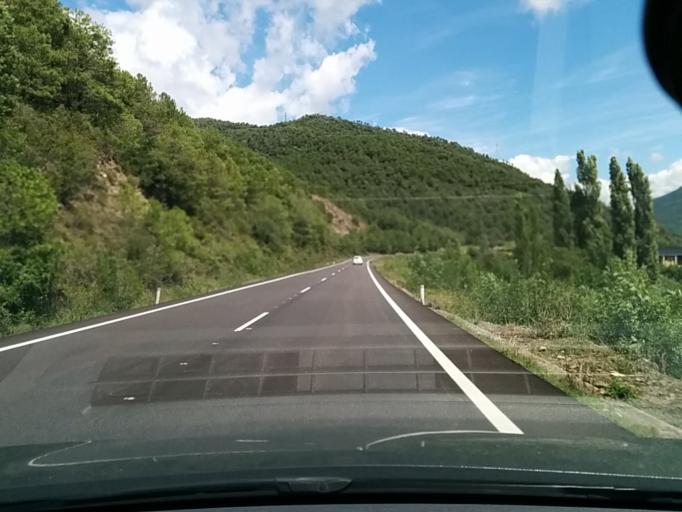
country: ES
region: Aragon
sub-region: Provincia de Huesca
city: Labuerda
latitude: 42.4614
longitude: 0.1358
